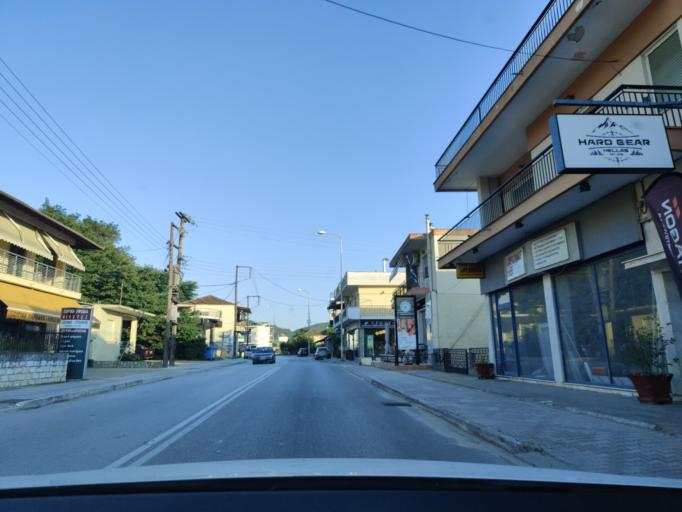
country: GR
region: East Macedonia and Thrace
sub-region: Nomos Kavalas
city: Amygdaleonas
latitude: 40.9653
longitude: 24.3563
